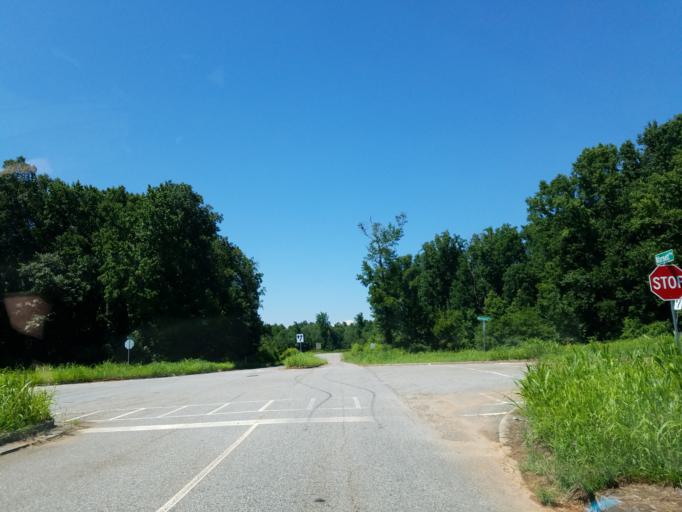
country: US
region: Georgia
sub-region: Forsyth County
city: Cumming
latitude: 34.2777
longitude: -84.0752
